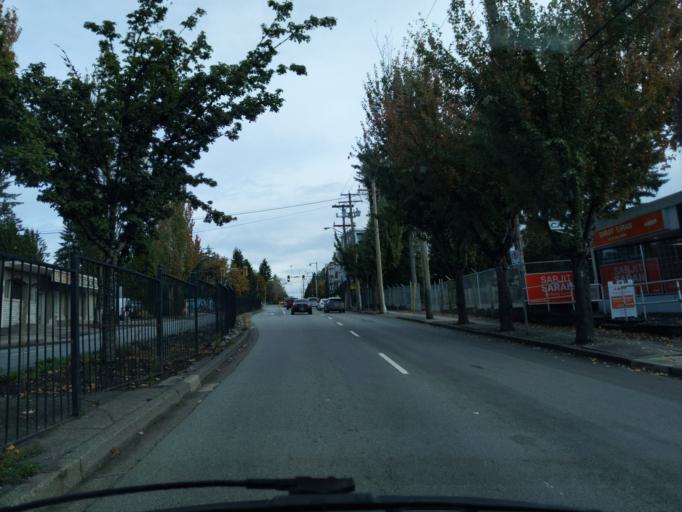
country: CA
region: British Columbia
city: New Westminster
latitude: 49.1988
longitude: -122.8442
